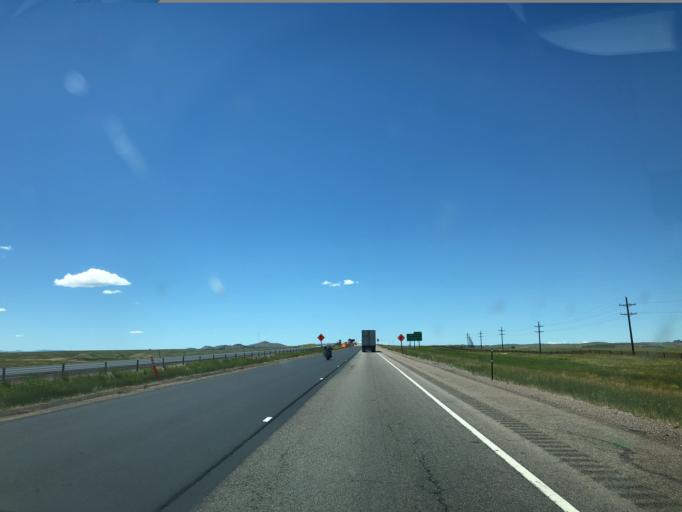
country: US
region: Wyoming
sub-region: Laramie County
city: Cheyenne
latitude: 41.0997
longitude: -105.0893
